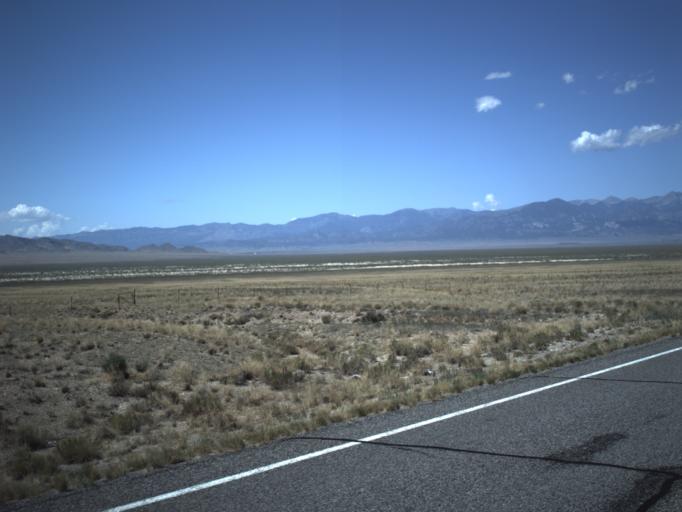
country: US
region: Nevada
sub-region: White Pine County
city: McGill
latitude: 39.0424
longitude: -113.8563
